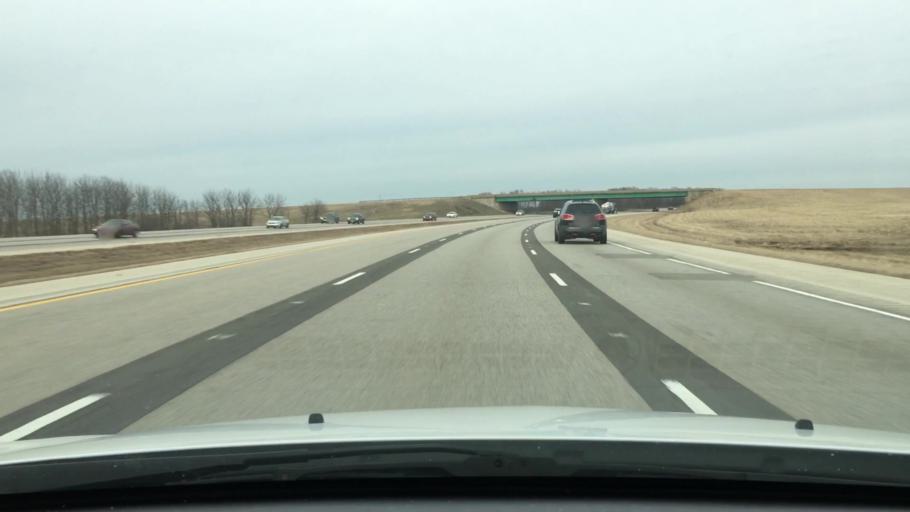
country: US
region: Illinois
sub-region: Sangamon County
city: Williamsville
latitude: 40.0175
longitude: -89.4980
